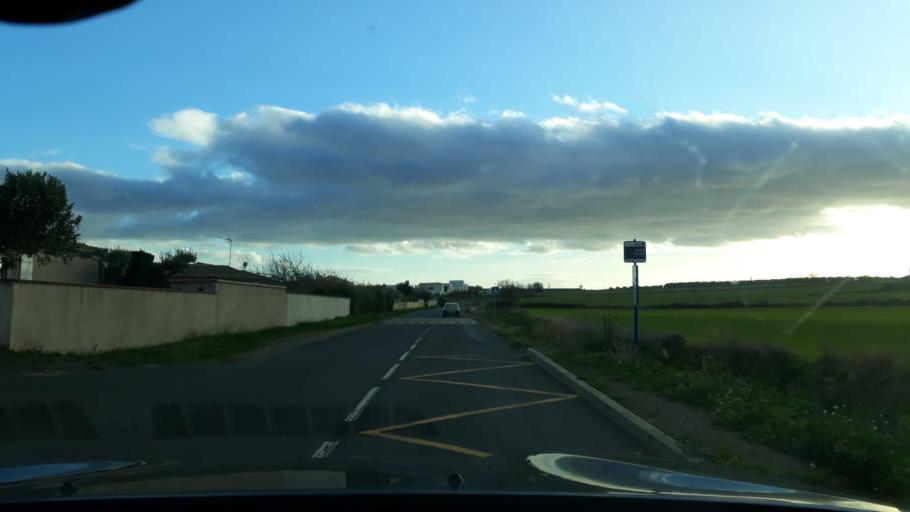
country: FR
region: Languedoc-Roussillon
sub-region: Departement de l'Herault
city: Colombiers
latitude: 43.3114
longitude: 3.1396
